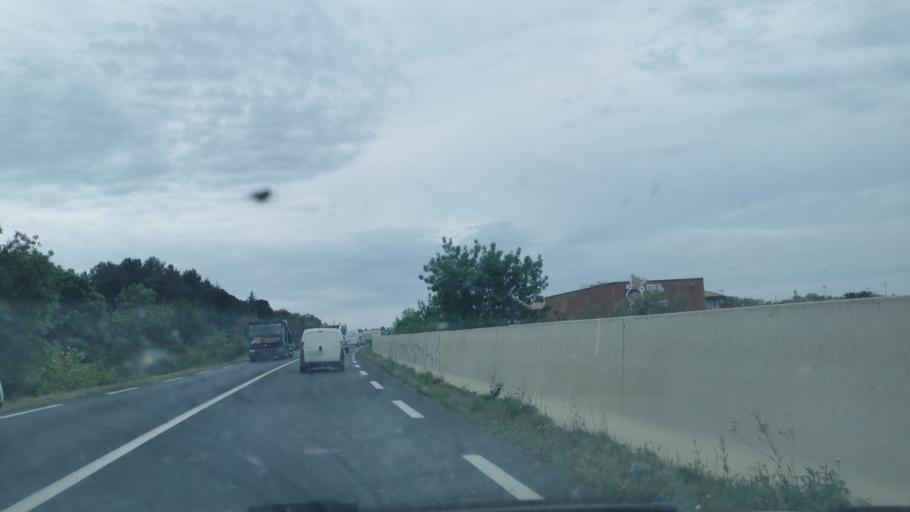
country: FR
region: Languedoc-Roussillon
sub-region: Departement de l'Herault
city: Balaruc-le-Vieux
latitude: 43.4660
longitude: 3.6924
